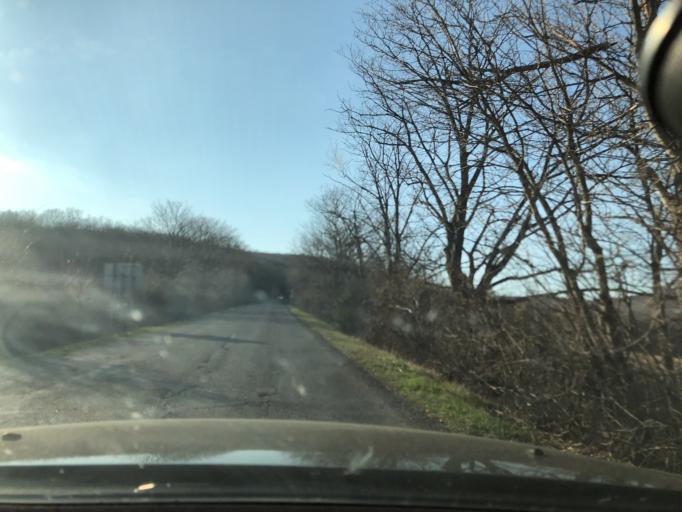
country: HU
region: Nograd
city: Paszto
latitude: 47.9145
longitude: 19.6435
